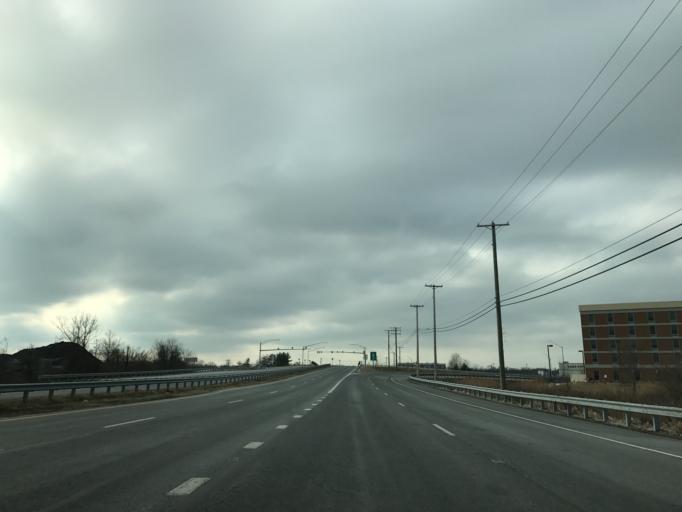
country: US
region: Maryland
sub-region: Harford County
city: Aberdeen
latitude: 39.4927
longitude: -76.1808
